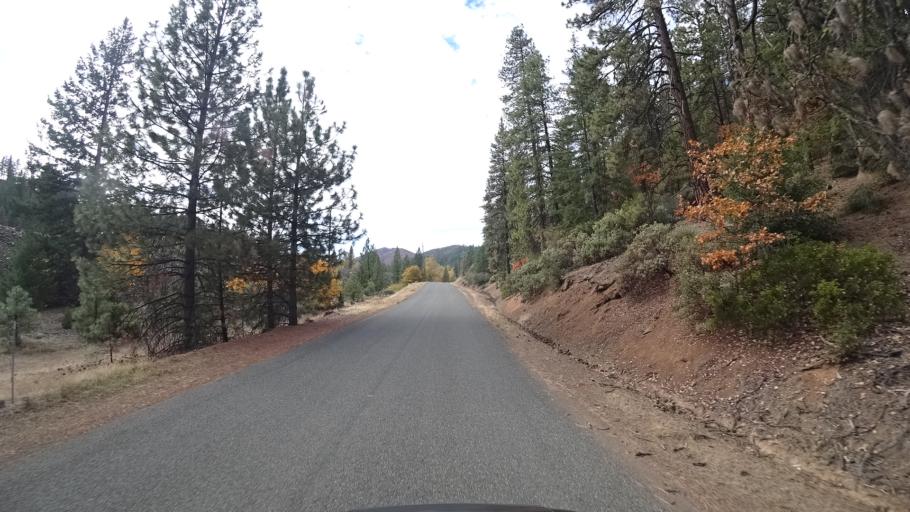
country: US
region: California
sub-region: Siskiyou County
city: Yreka
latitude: 41.6828
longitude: -122.8261
